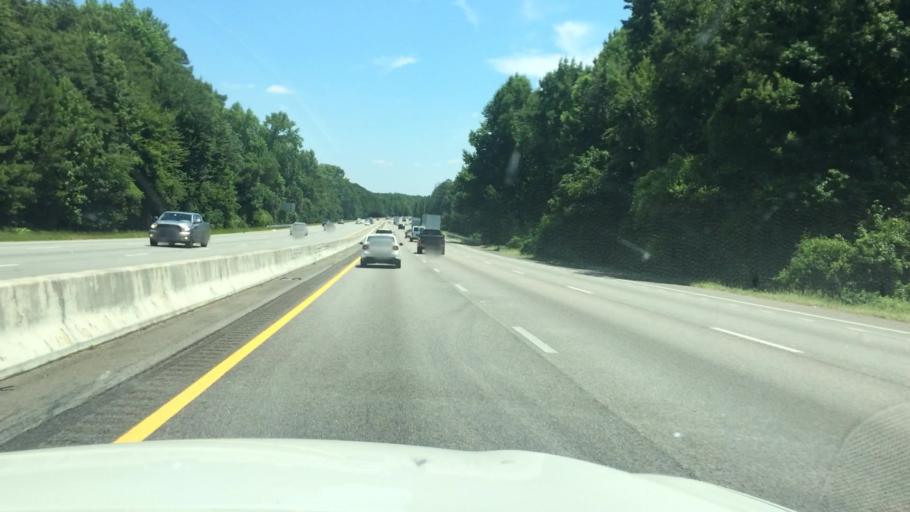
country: US
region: South Carolina
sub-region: Richland County
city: Forest Acres
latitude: 34.0694
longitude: -81.0158
